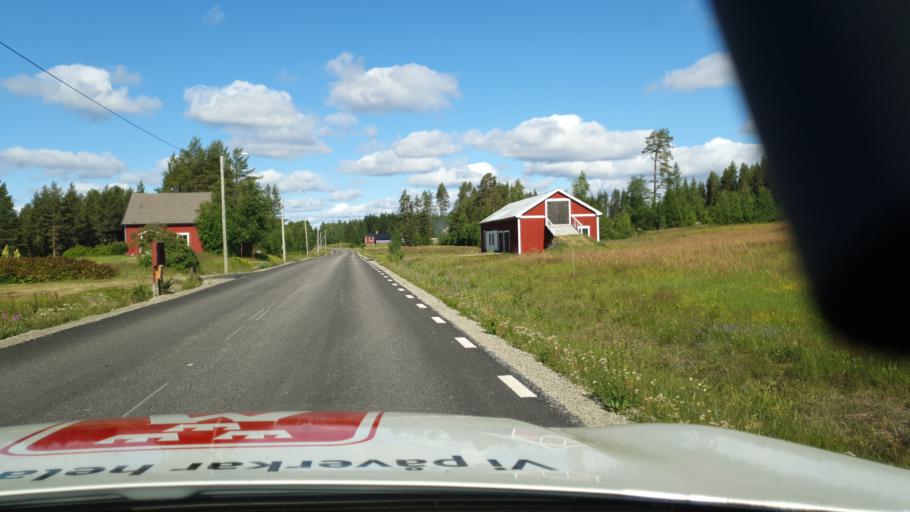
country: SE
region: Vaesterbotten
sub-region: Lycksele Kommun
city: Lycksele
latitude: 64.7624
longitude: 19.0587
